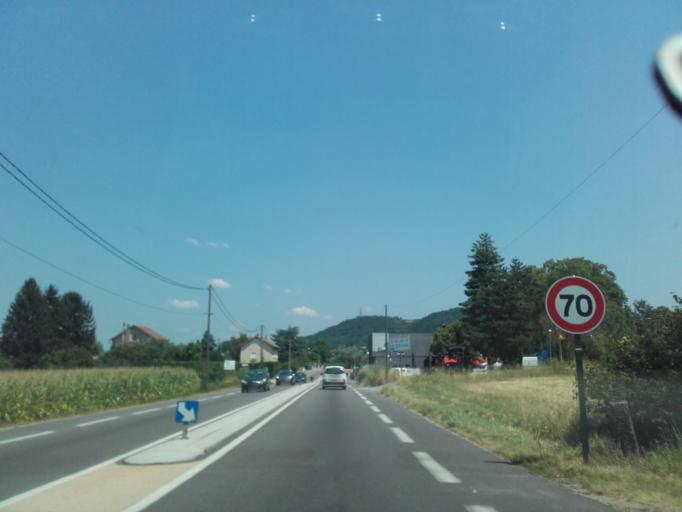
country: FR
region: Rhone-Alpes
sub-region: Departement de l'Isere
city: Saint-Savin
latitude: 45.6233
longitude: 5.2823
